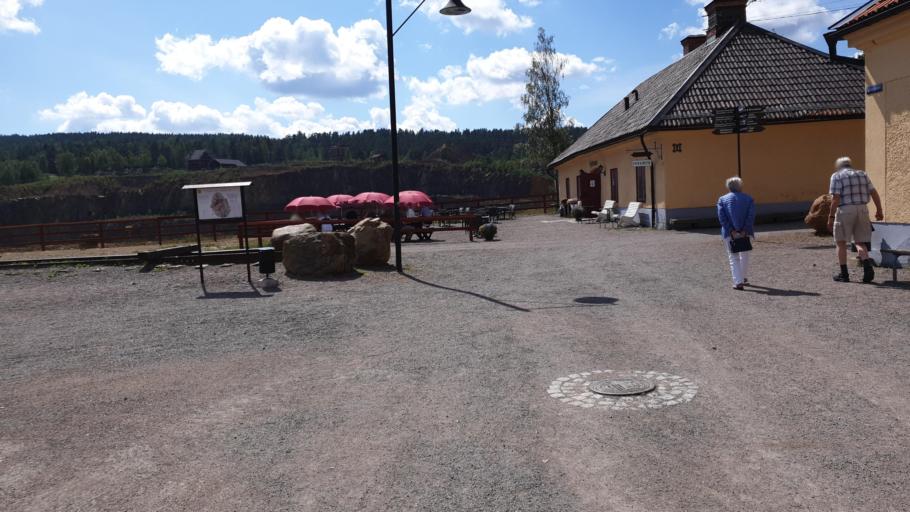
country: SE
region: Dalarna
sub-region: Faluns Kommun
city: Falun
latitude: 60.6005
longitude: 15.6157
